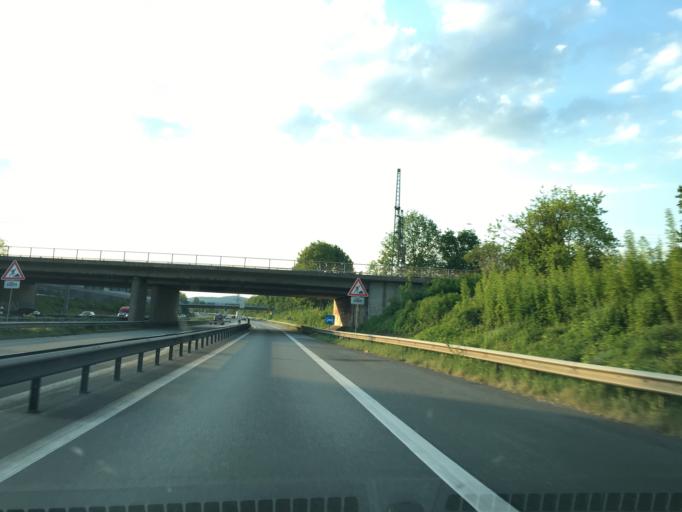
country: DE
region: North Rhine-Westphalia
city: Bad Oeynhausen
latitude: 52.2080
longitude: 8.8390
